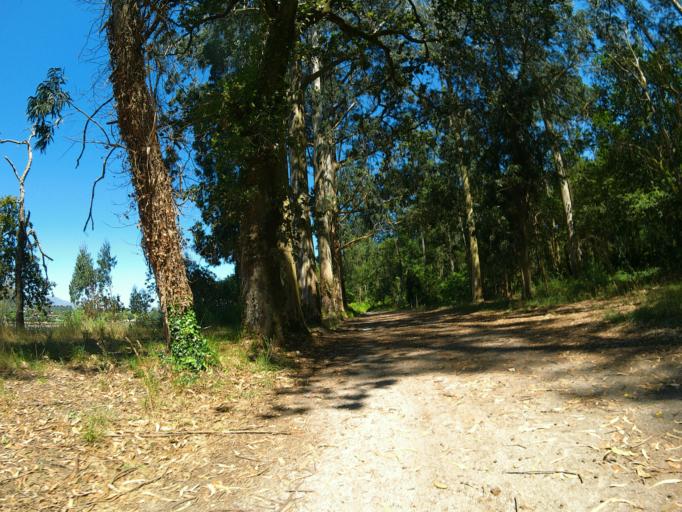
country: PT
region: Viana do Castelo
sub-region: Viana do Castelo
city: Darque
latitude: 41.6970
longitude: -8.7536
